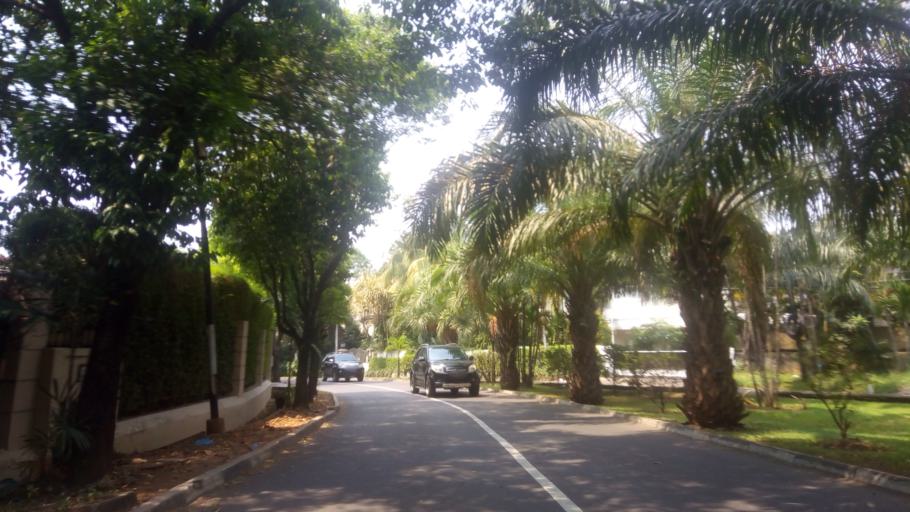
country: ID
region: Jakarta Raya
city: Jakarta
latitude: -6.2353
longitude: 106.8346
